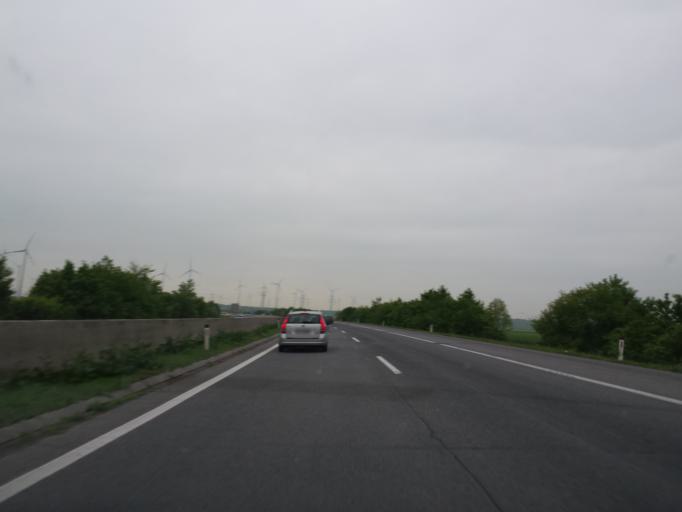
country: AT
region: Burgenland
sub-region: Politischer Bezirk Neusiedl am See
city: Nickelsdorf
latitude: 47.9279
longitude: 17.0915
